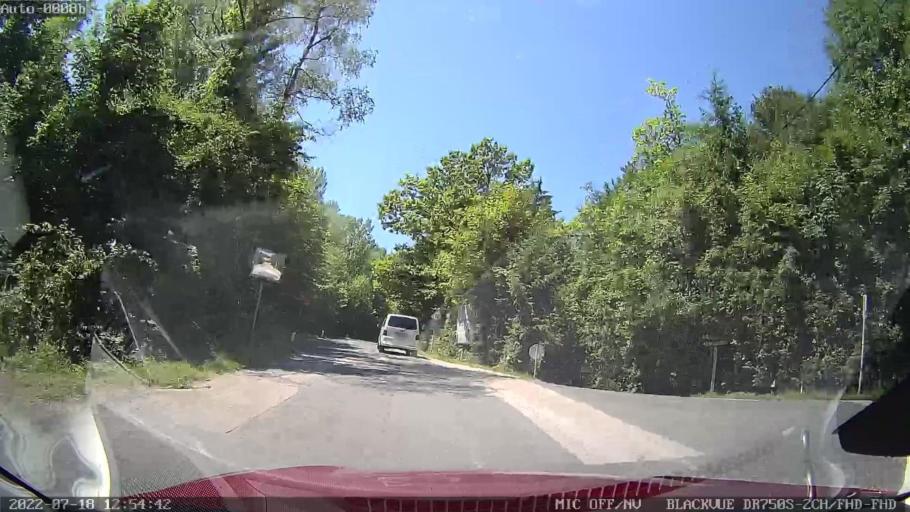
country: SI
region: Dobrova-Horjul-Polhov Gradec
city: Dobrova
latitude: 46.0761
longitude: 14.4397
